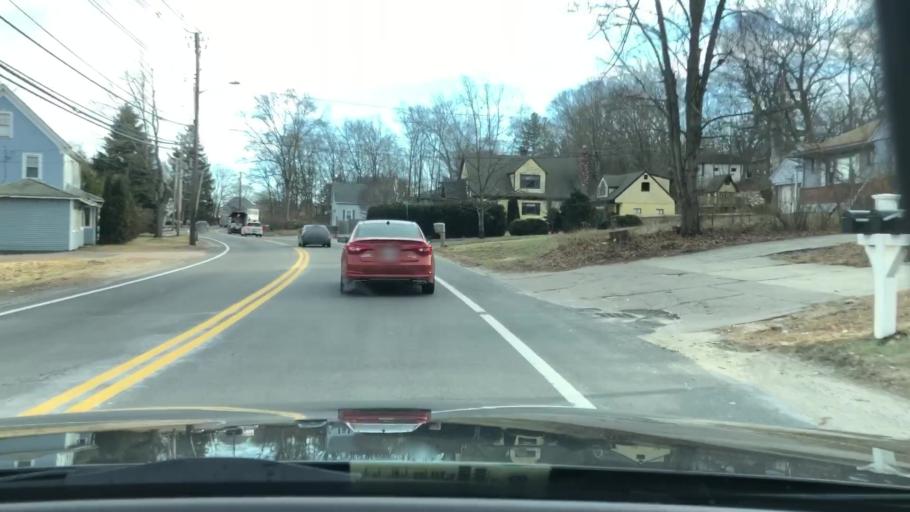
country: US
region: Massachusetts
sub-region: Worcester County
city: Milford
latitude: 42.1229
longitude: -71.5153
